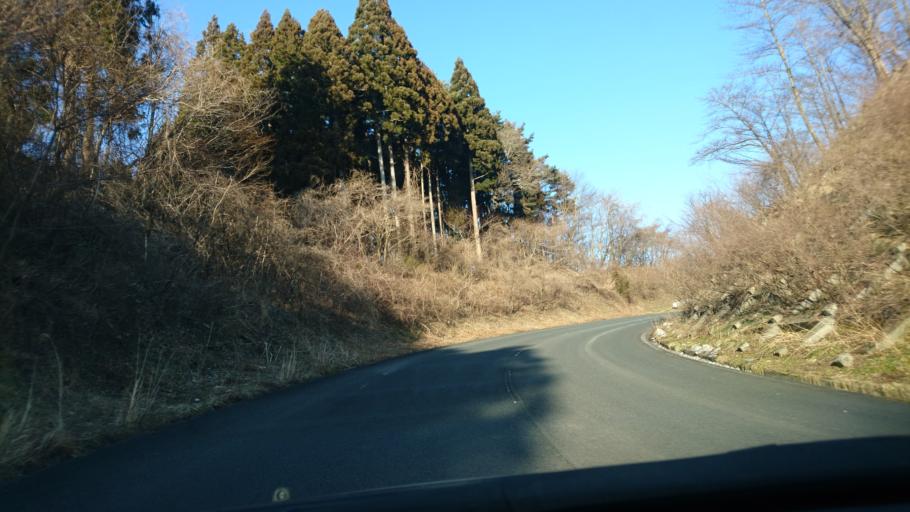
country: JP
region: Iwate
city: Ichinoseki
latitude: 38.8726
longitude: 141.3876
